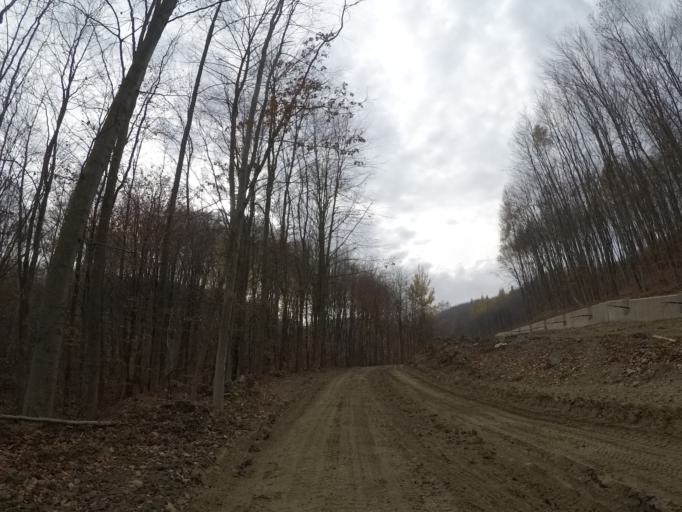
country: SK
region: Presovsky
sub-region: Okres Presov
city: Presov
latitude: 48.9800
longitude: 21.2171
